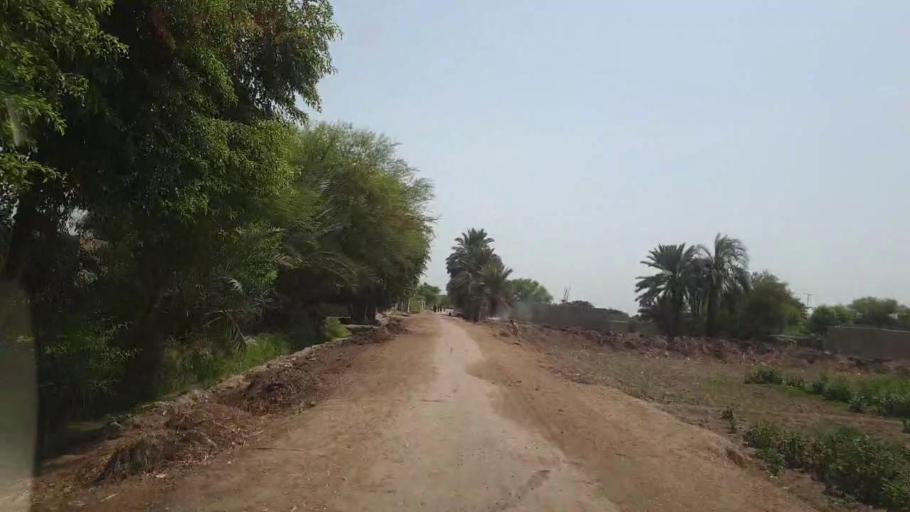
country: PK
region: Sindh
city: Sobhadero
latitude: 27.4386
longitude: 68.4016
